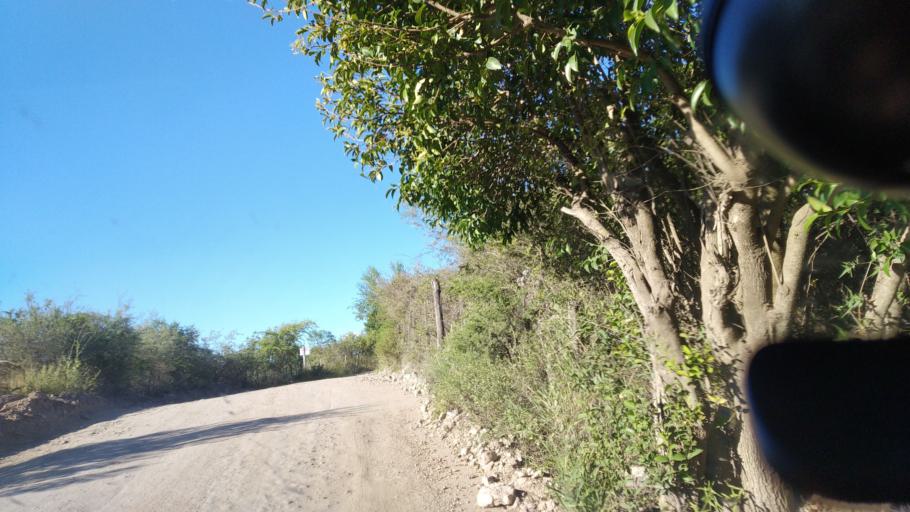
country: AR
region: Cordoba
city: Mina Clavero
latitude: -31.7263
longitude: -64.9940
